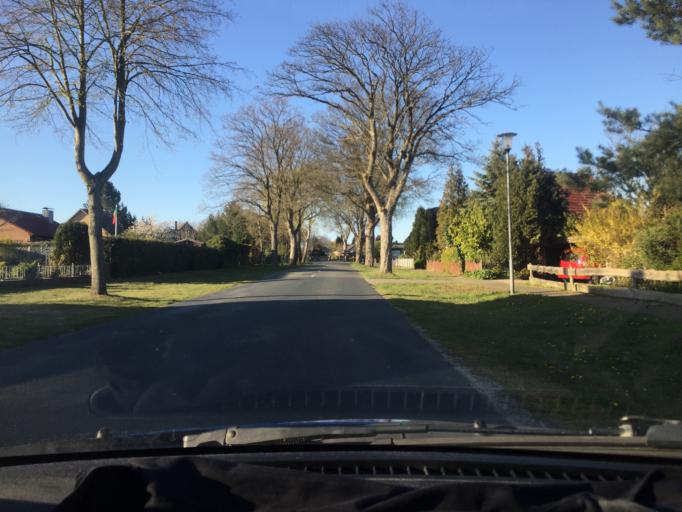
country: DE
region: Lower Saxony
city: Weste
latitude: 53.0623
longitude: 10.7244
